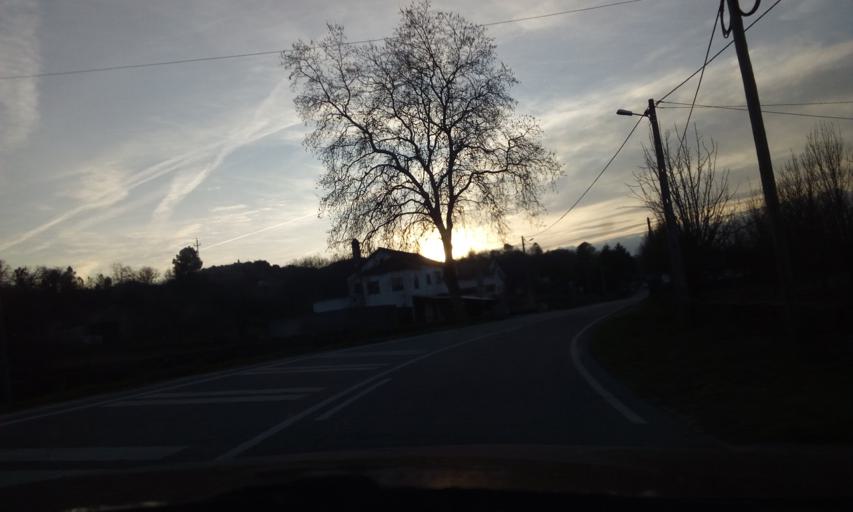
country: PT
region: Guarda
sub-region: Guarda
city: Sequeira
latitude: 40.5958
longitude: -7.1233
